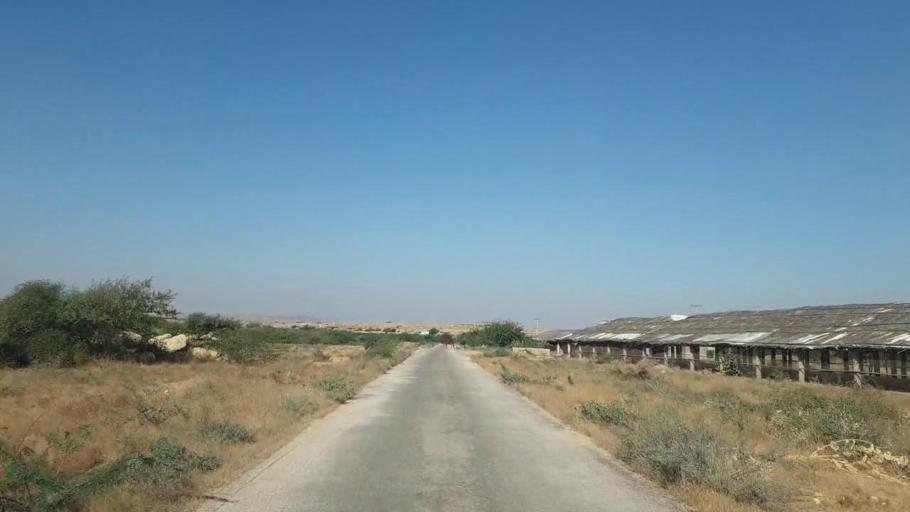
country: PK
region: Sindh
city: Gharo
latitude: 25.0855
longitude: 67.5361
